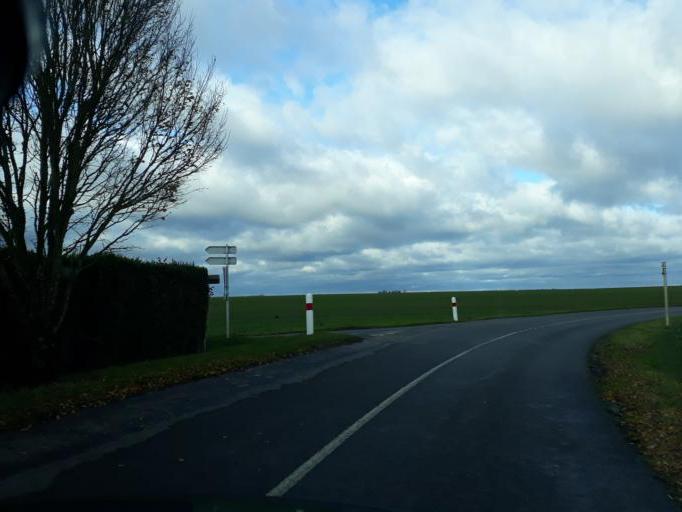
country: FR
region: Centre
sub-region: Departement du Loir-et-Cher
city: Suevres
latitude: 47.7436
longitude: 1.4218
